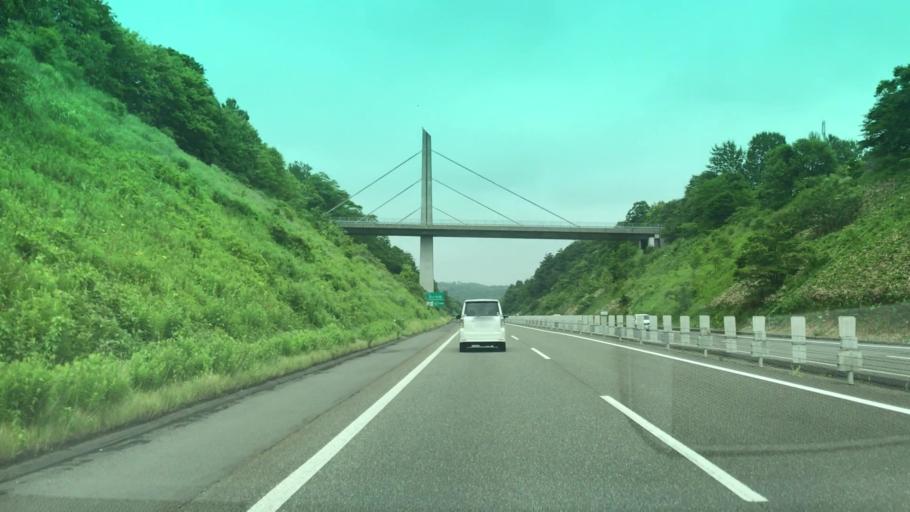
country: JP
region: Hokkaido
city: Tomakomai
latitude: 42.6232
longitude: 141.4798
